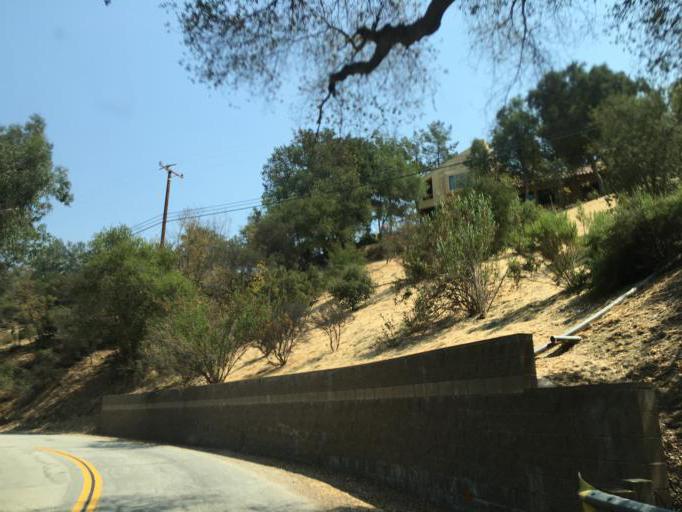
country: US
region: California
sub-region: Los Angeles County
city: Topanga
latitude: 34.1160
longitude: -118.5863
